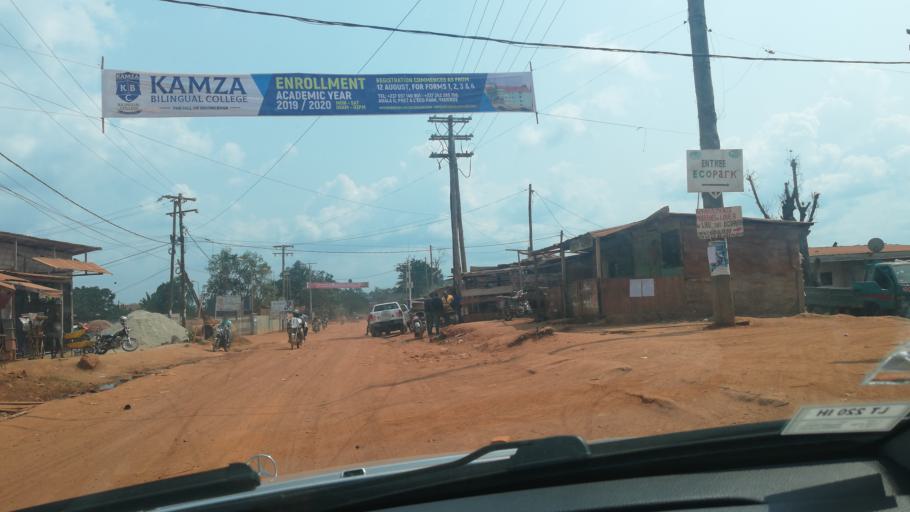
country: CM
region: Centre
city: Yaounde
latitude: 3.7842
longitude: 11.4903
